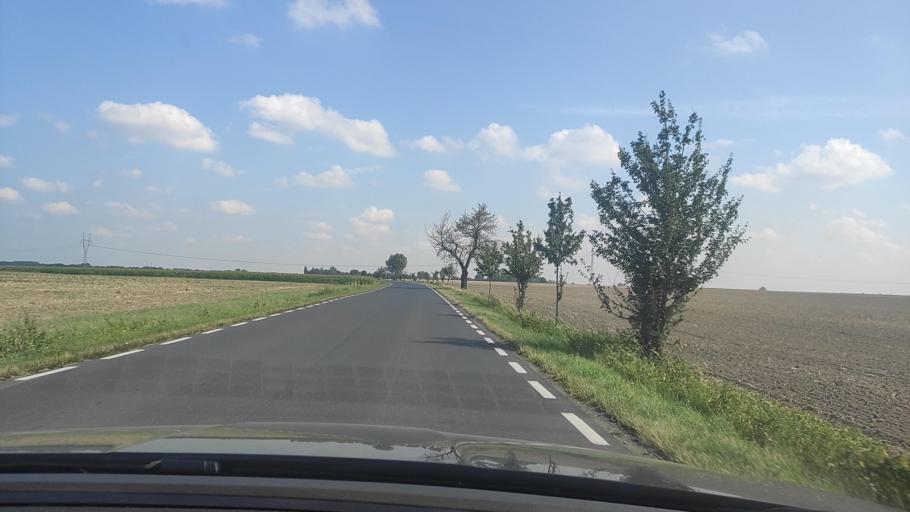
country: PL
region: Greater Poland Voivodeship
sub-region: Powiat poznanski
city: Kostrzyn
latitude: 52.4335
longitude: 17.1617
